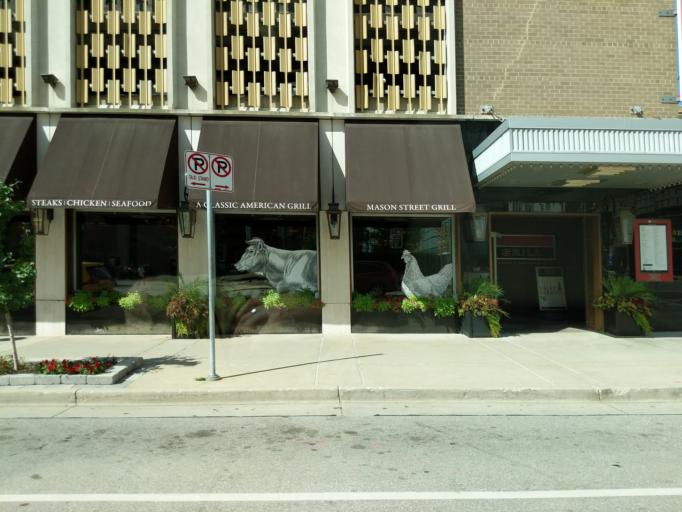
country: US
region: Wisconsin
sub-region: Milwaukee County
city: Milwaukee
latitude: 43.0398
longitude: -87.9055
